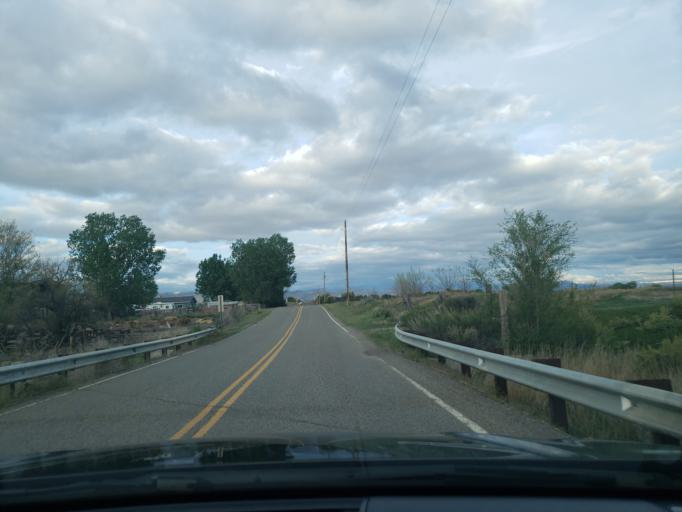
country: US
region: Colorado
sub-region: Mesa County
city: Fruita
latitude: 39.2220
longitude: -108.7057
